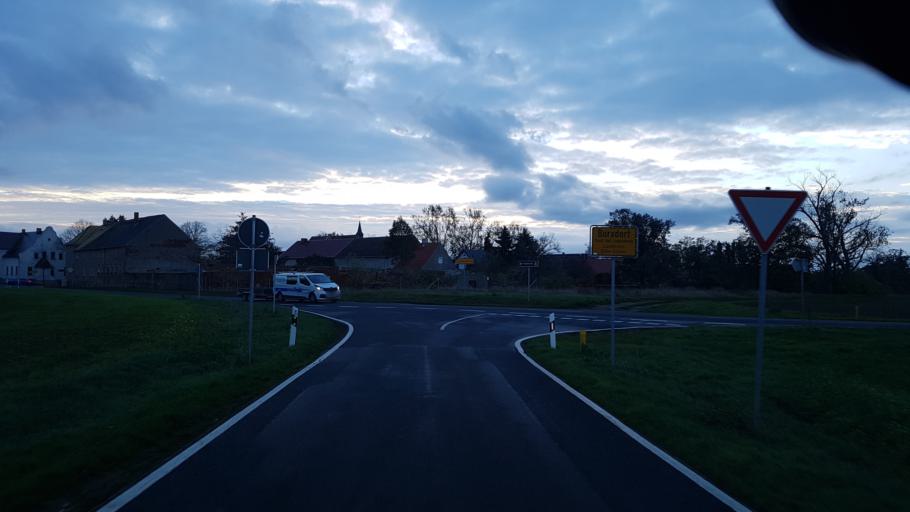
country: DE
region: Brandenburg
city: Muhlberg
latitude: 51.4607
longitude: 13.2547
